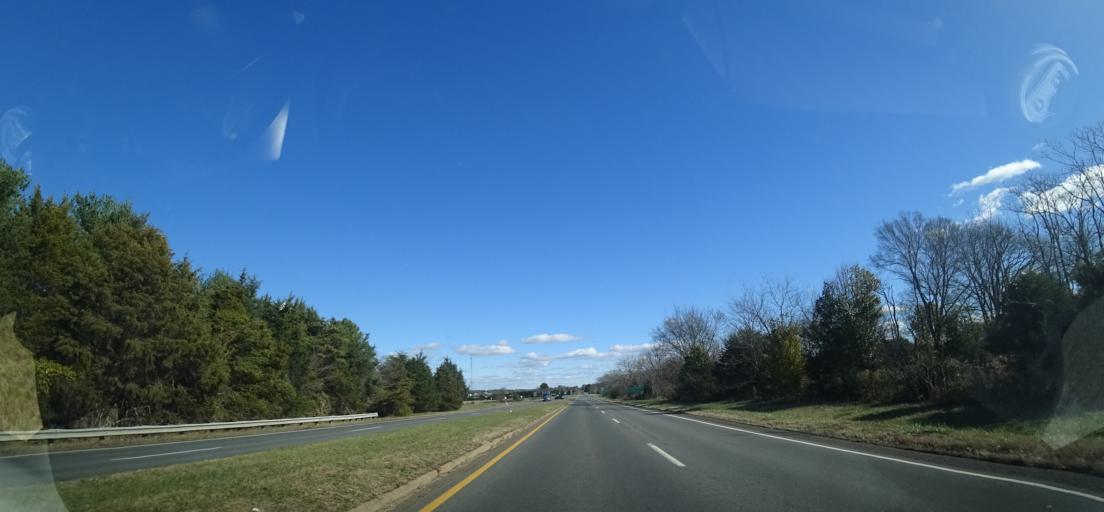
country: US
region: Virginia
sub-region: Culpeper County
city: Culpeper
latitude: 38.4894
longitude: -77.9362
